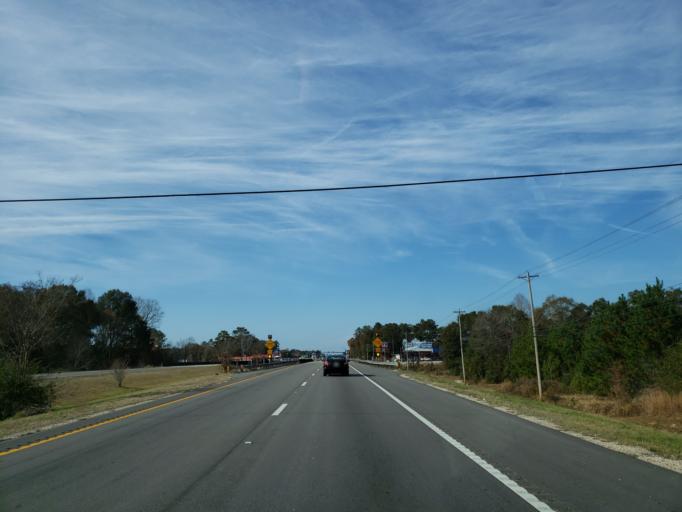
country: US
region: Mississippi
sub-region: Forrest County
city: Rawls Springs
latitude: 31.3879
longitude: -89.3748
